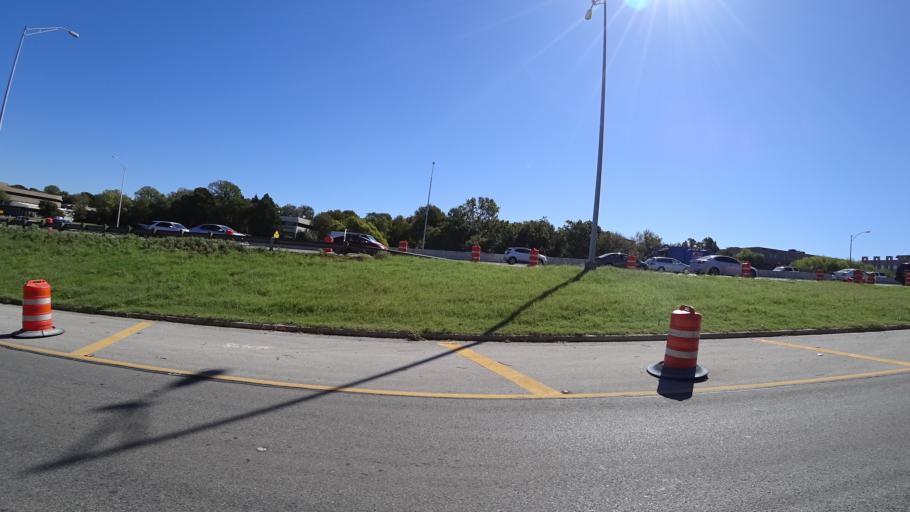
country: US
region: Texas
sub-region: Travis County
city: Austin
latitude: 30.2384
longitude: -97.7389
